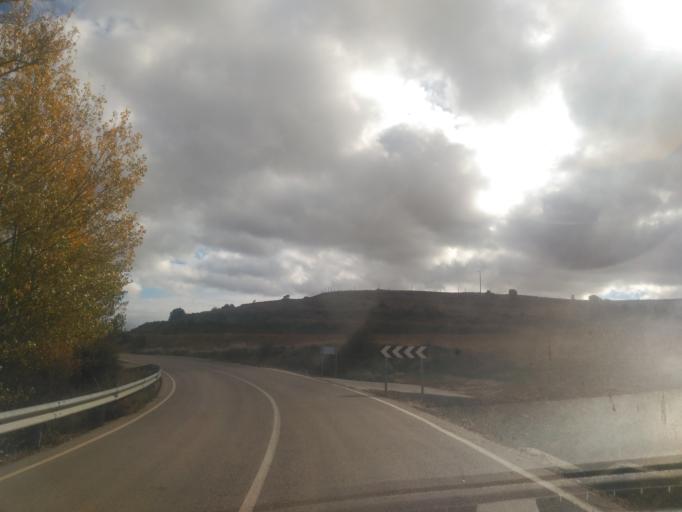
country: ES
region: Castille and Leon
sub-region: Provincia de Soria
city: Alcubilla de Avellaneda
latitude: 41.7550
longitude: -3.2615
